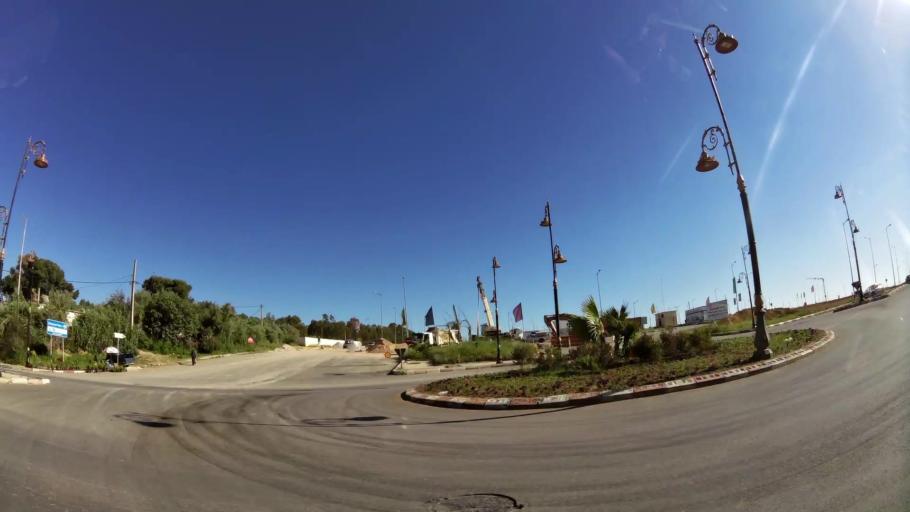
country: MA
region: Fes-Boulemane
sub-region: Fes
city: Fes
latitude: 33.9912
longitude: -5.0214
